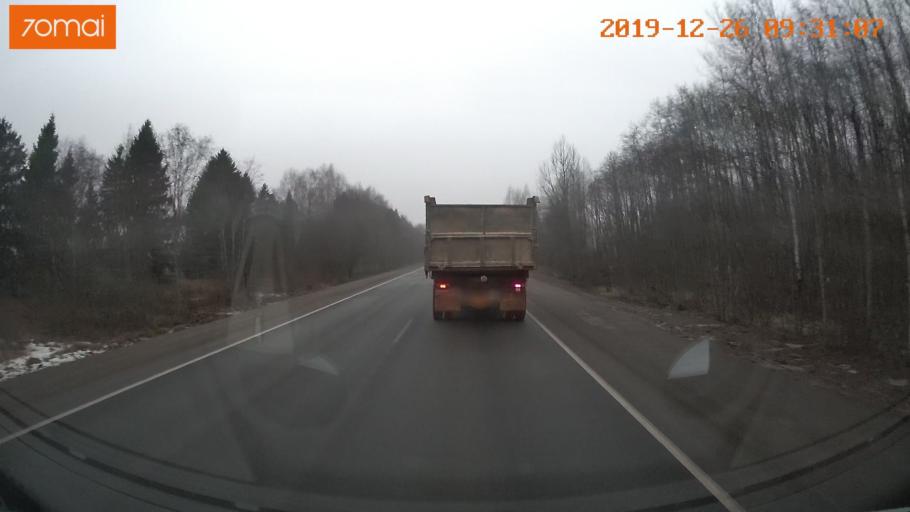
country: RU
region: Vologda
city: Gryazovets
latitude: 59.0666
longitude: 40.1313
